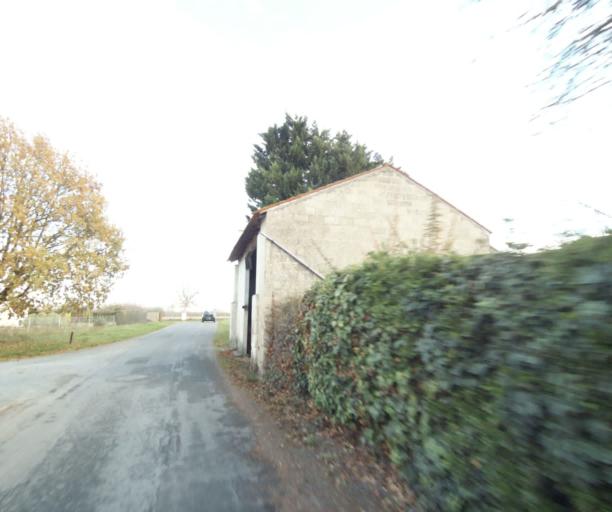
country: FR
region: Poitou-Charentes
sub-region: Departement de la Charente-Maritime
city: Les Gonds
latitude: 45.7099
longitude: -0.6116
